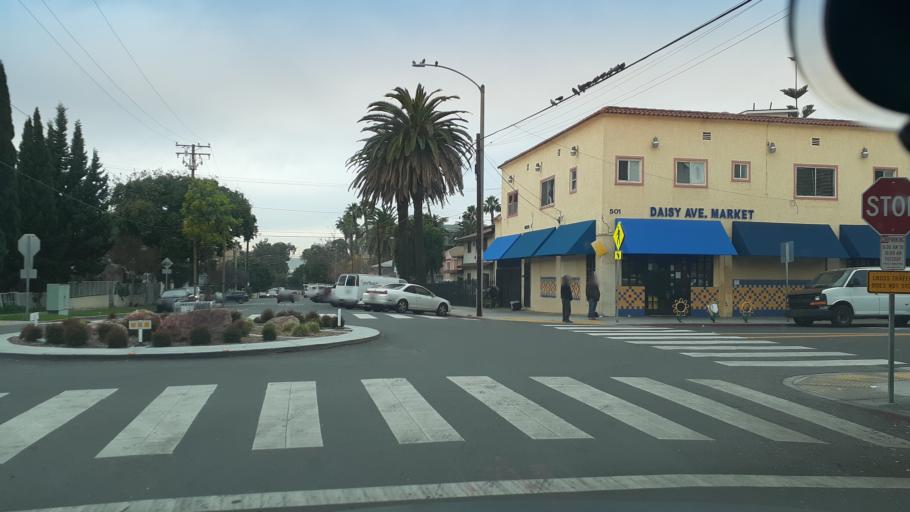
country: US
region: California
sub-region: Los Angeles County
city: Long Beach
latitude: 33.7730
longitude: -118.1992
